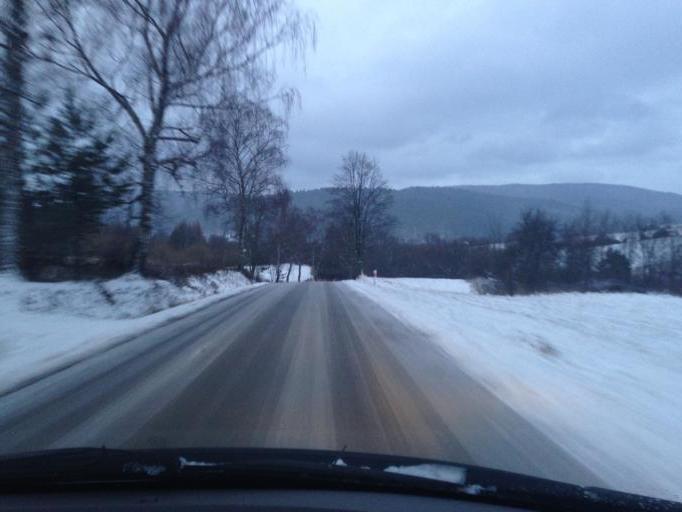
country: PL
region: Subcarpathian Voivodeship
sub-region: Powiat jasielski
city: Krempna
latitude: 49.5203
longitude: 21.5025
